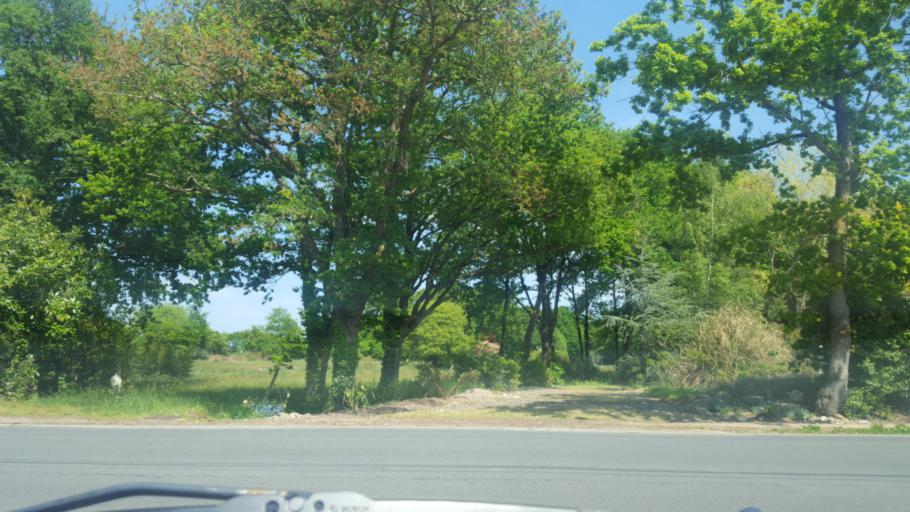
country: FR
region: Pays de la Loire
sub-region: Departement de la Loire-Atlantique
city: La Limouziniere
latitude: 47.0212
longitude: -1.5691
